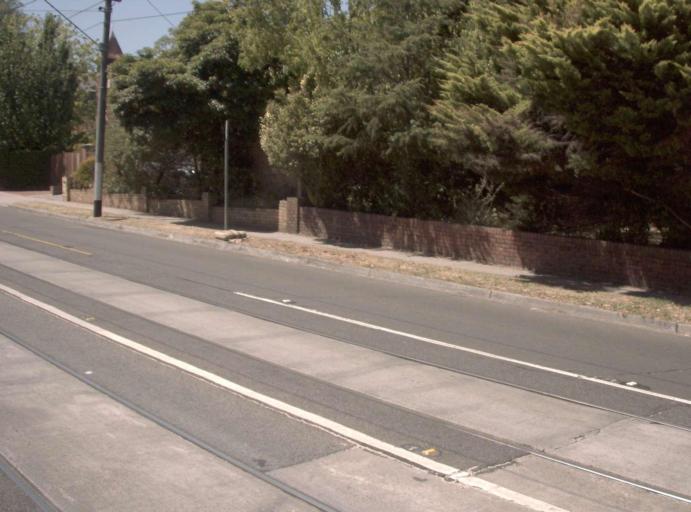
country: AU
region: Victoria
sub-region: Boroondara
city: Canterbury
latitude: -37.8342
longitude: 145.0816
